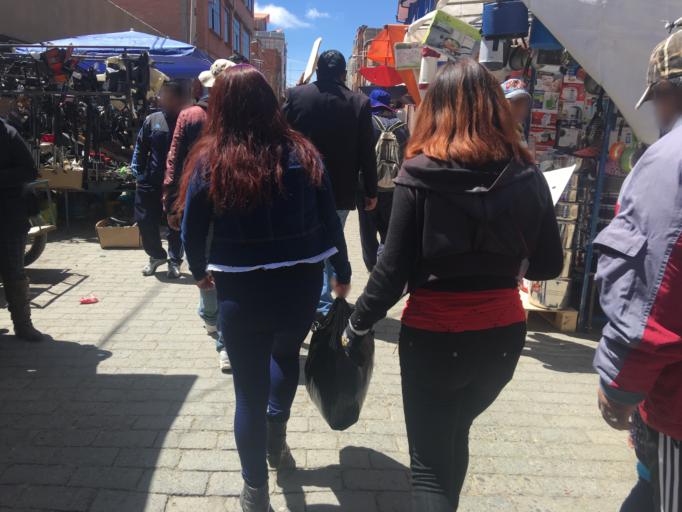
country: BO
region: La Paz
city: La Paz
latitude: -16.4968
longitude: -68.1671
